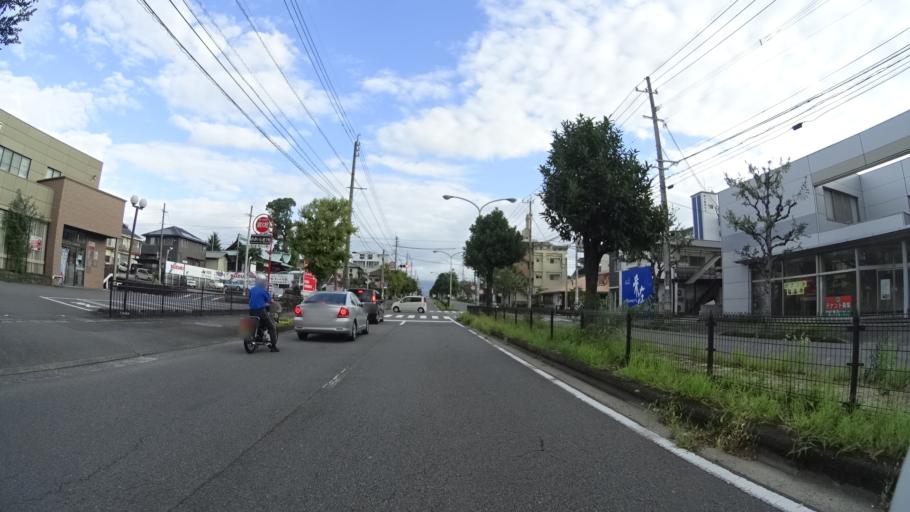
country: JP
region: Oita
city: Beppu
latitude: 33.2938
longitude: 131.4957
